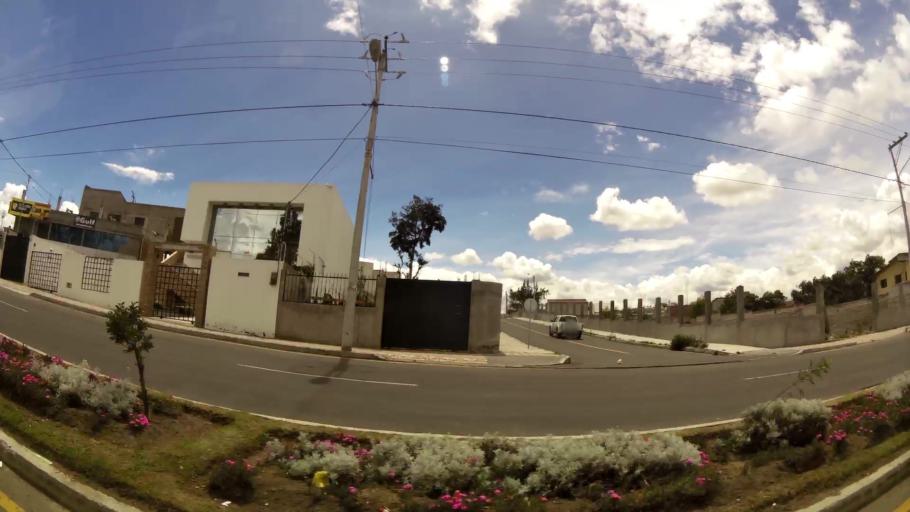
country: EC
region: Tungurahua
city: Ambato
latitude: -1.2603
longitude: -78.6113
